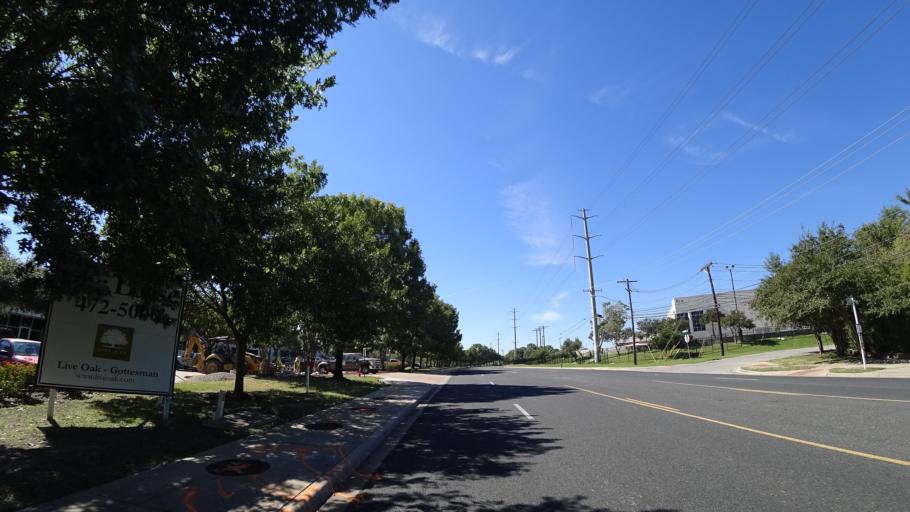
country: US
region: Texas
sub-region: Travis County
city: Austin
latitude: 30.2170
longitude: -97.6850
